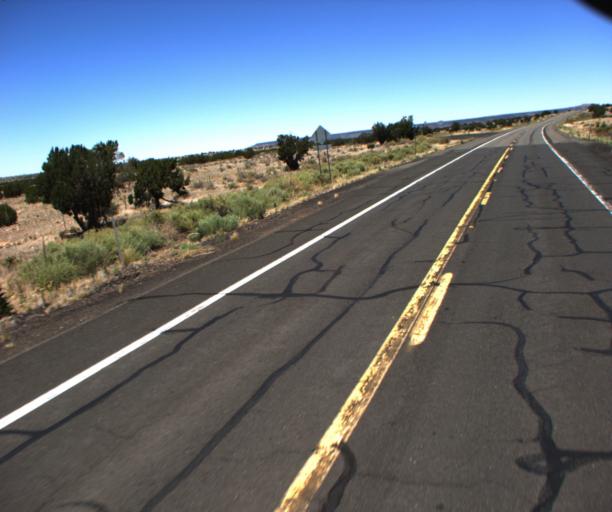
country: US
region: Arizona
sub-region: Coconino County
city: LeChee
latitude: 34.7719
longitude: -111.0068
